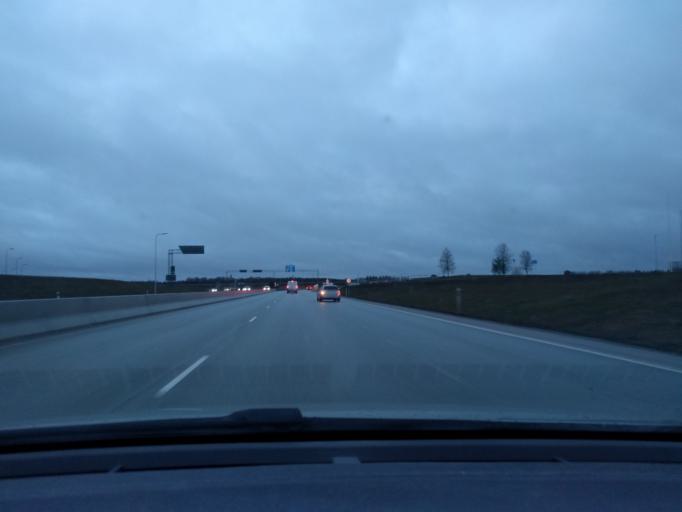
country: EE
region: Harju
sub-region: Rae vald
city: Jueri
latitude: 59.3568
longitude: 24.8885
